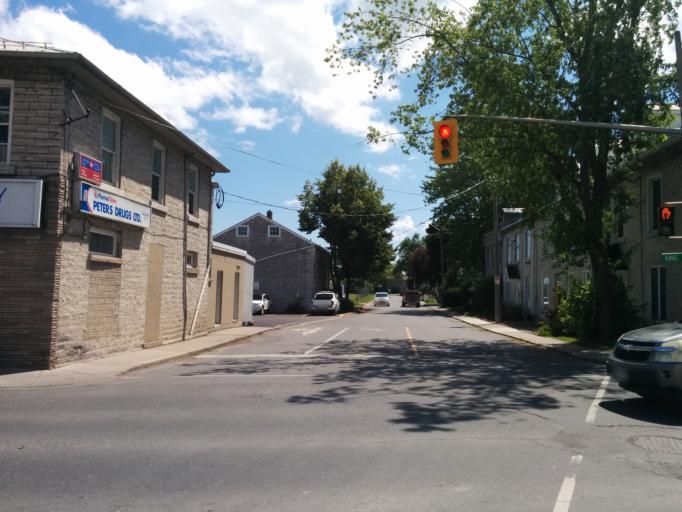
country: CA
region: Ontario
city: Kingston
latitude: 44.2210
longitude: -76.5177
